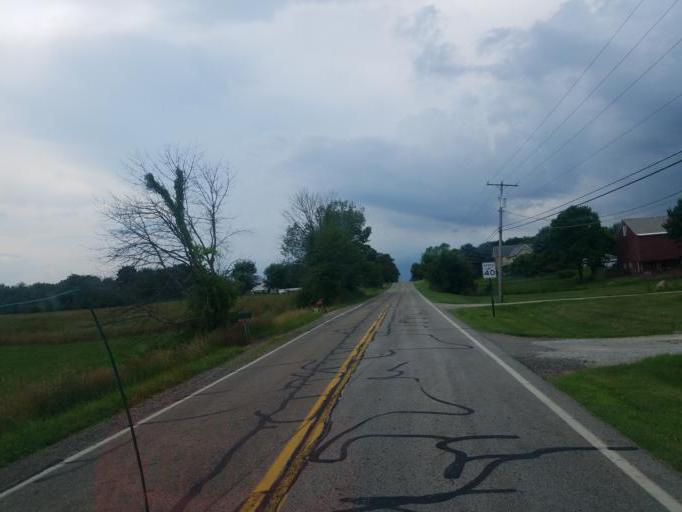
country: US
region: Ohio
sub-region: Stark County
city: Hartville
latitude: 41.0297
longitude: -81.2856
